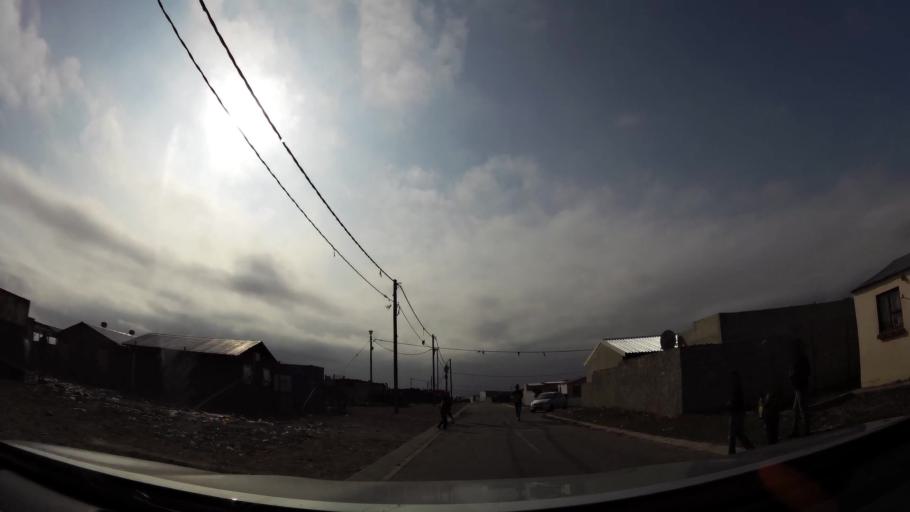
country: ZA
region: Eastern Cape
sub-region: Nelson Mandela Bay Metropolitan Municipality
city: Port Elizabeth
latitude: -33.9160
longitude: 25.5381
